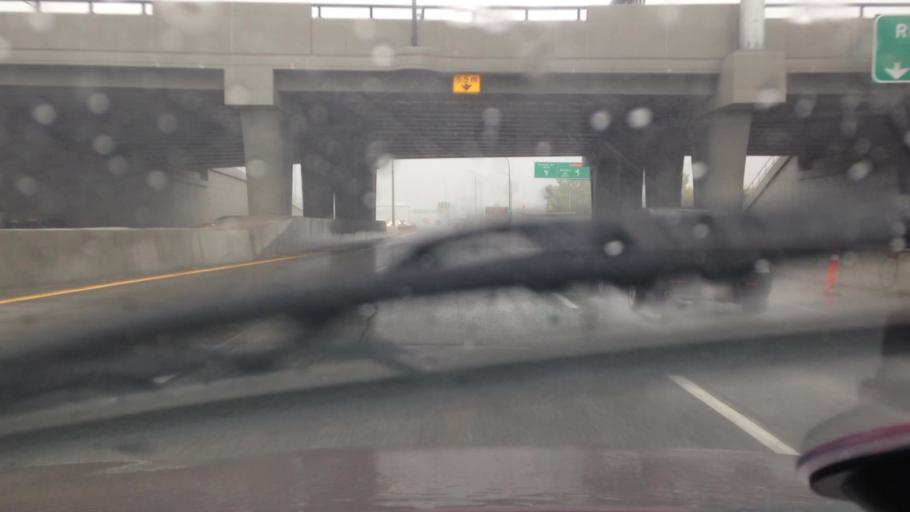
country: CA
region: Alberta
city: Calgary
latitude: 51.0166
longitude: -114.1181
